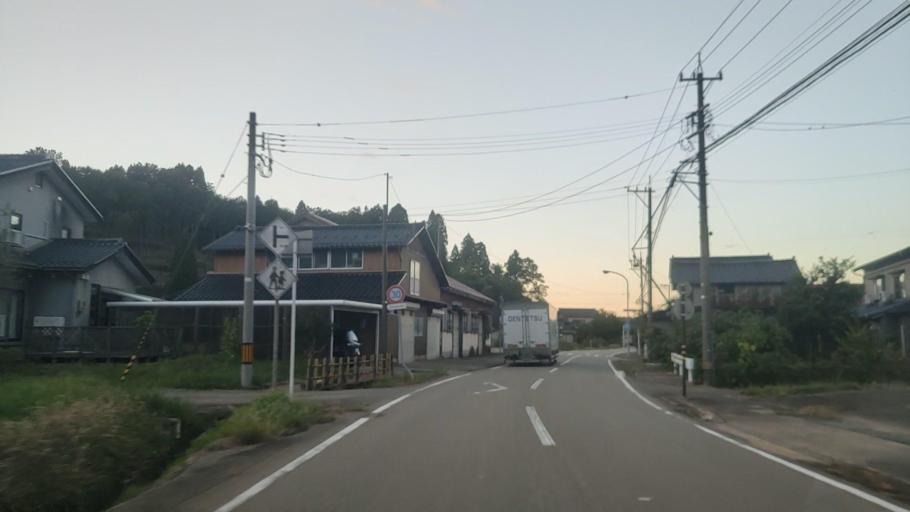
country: JP
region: Ishikawa
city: Tsubata
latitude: 36.6529
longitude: 136.7590
